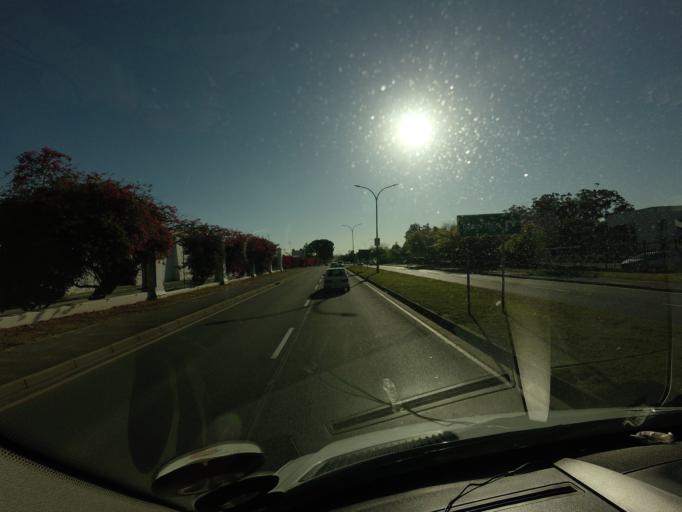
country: ZA
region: Western Cape
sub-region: Cape Winelands District Municipality
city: Stellenbosch
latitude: -33.9439
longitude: 18.8354
